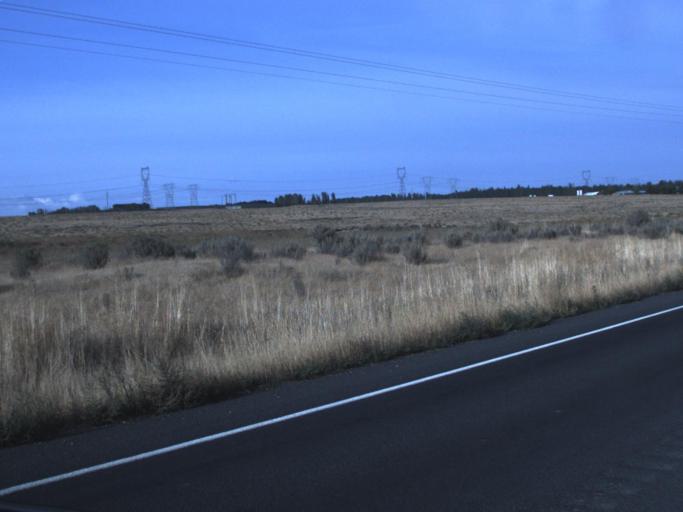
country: US
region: Oregon
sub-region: Morrow County
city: Boardman
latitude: 45.9306
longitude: -119.6191
